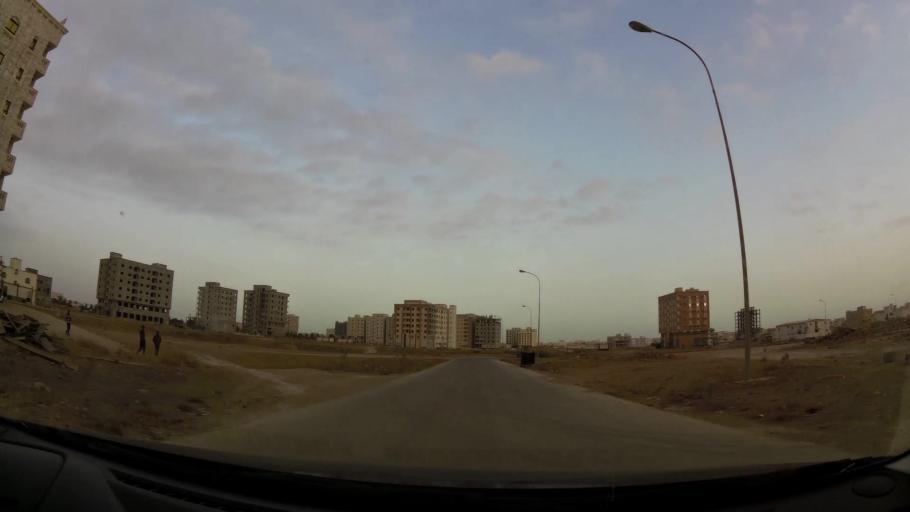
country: OM
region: Zufar
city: Salalah
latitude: 17.0270
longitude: 54.0287
